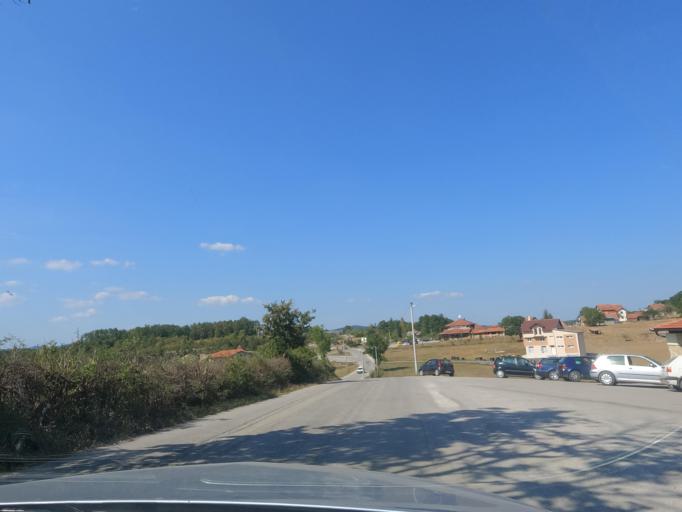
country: RS
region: Central Serbia
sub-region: Zlatiborski Okrug
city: Cajetina
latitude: 43.7898
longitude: 19.7657
